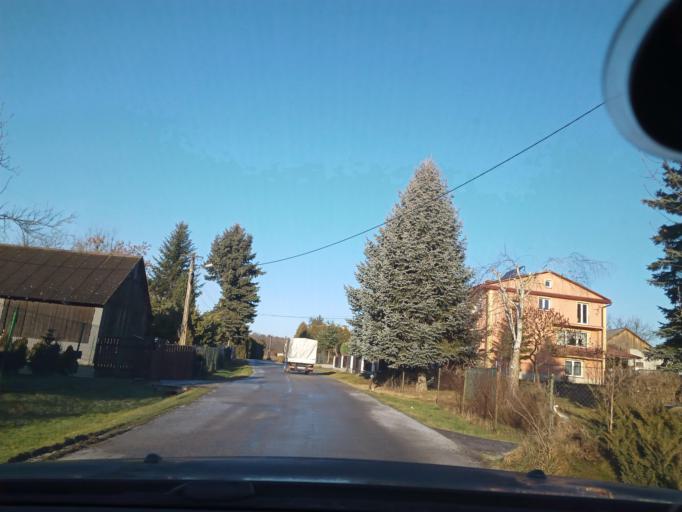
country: PL
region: Lesser Poland Voivodeship
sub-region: Powiat krakowski
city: Michalowice
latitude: 50.1909
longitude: 20.0263
